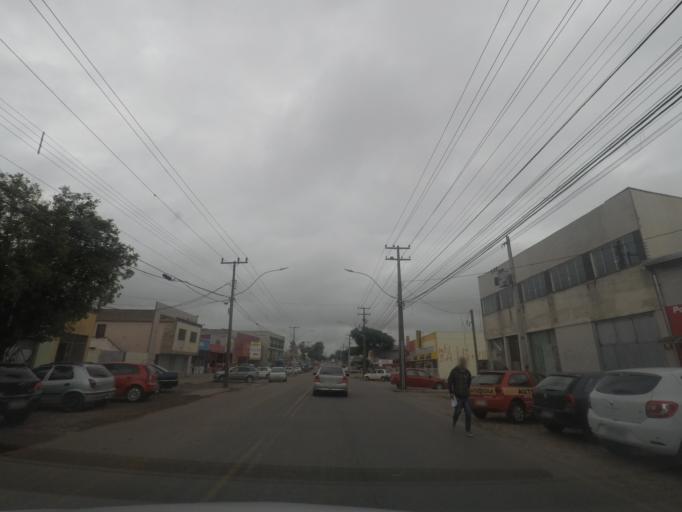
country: BR
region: Parana
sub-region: Piraquara
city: Piraquara
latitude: -25.4485
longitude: -49.0671
